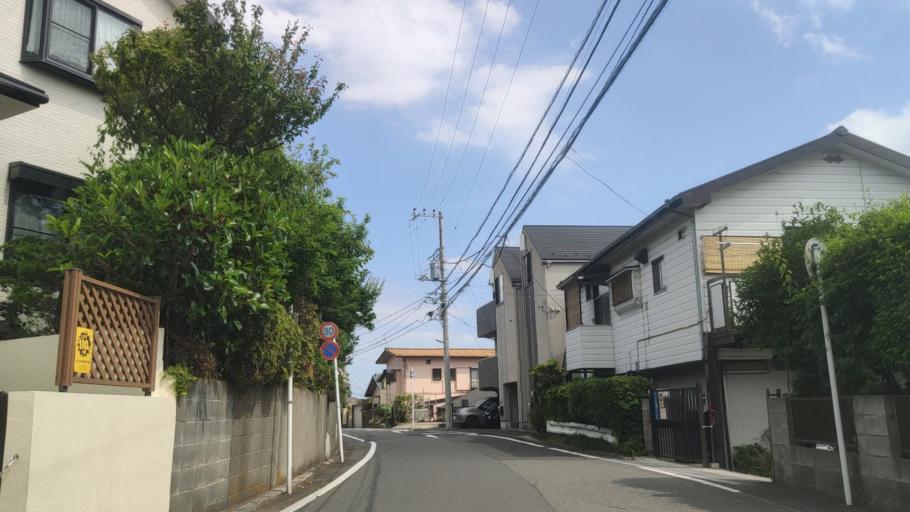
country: JP
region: Kanagawa
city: Yokohama
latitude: 35.4299
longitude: 139.6259
